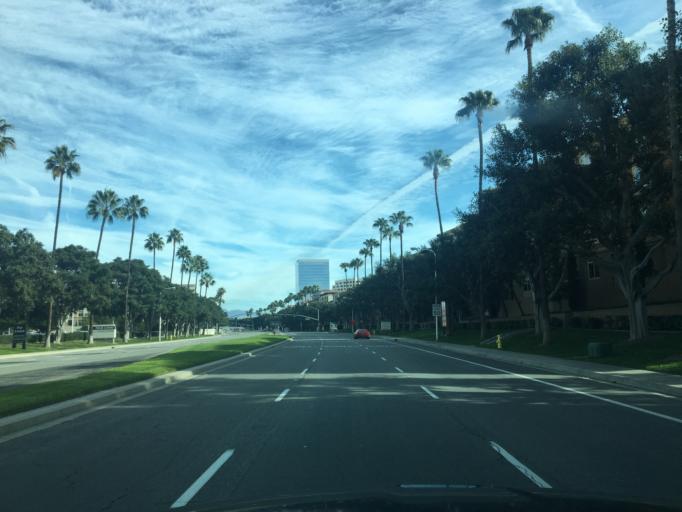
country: US
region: California
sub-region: Orange County
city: Laguna Woods
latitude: 33.6555
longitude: -117.7549
